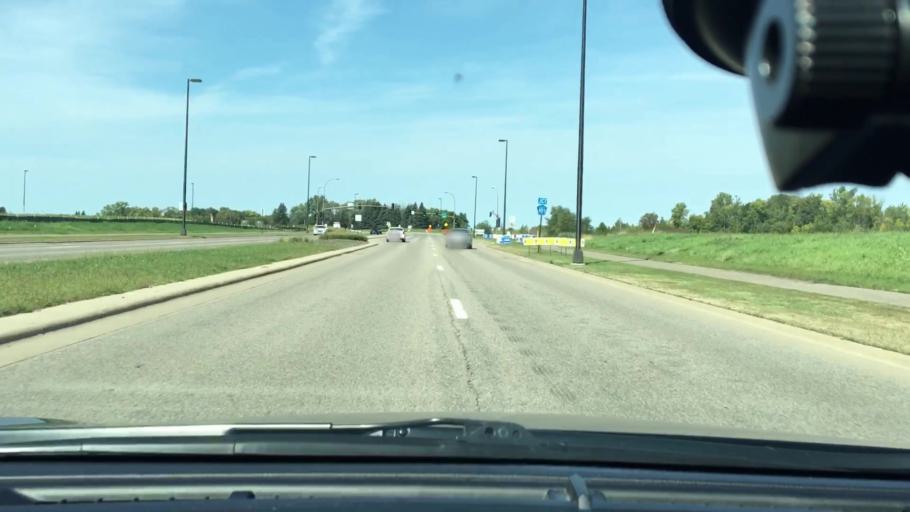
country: US
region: Minnesota
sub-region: Hennepin County
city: Corcoran
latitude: 45.0845
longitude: -93.5150
